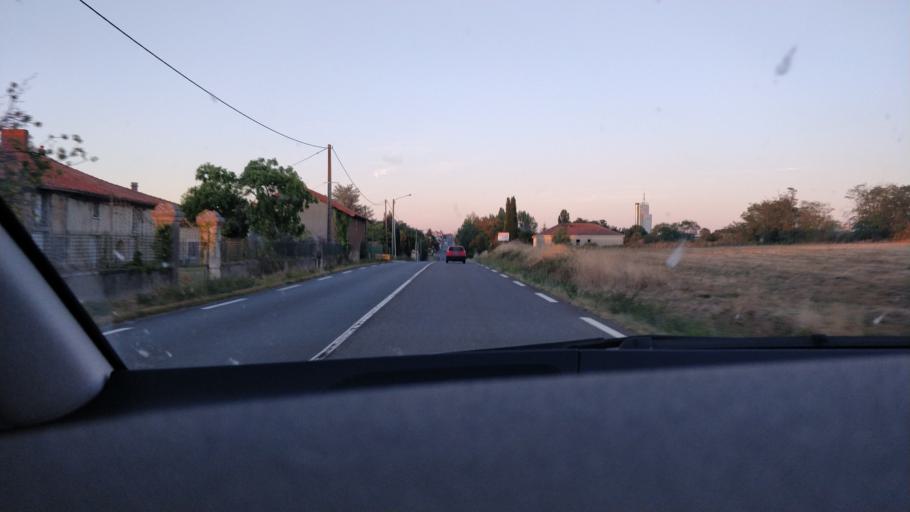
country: FR
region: Poitou-Charentes
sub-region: Departement de la Charente
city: Loubert
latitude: 45.8804
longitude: 0.5682
